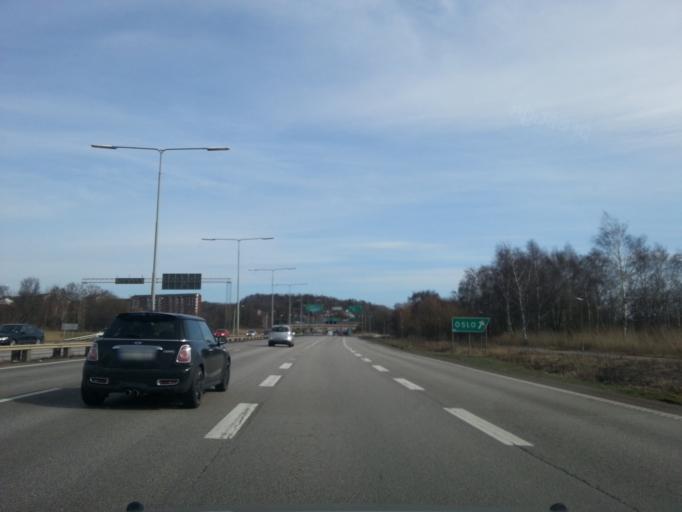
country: SE
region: Vaestra Goetaland
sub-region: Goteborg
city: Goeteborg
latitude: 57.7249
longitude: 11.9634
